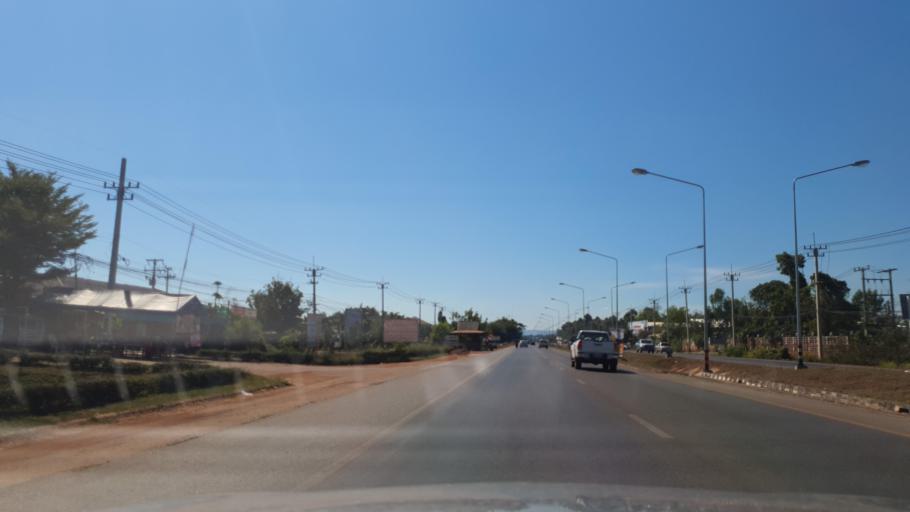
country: TH
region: Sakon Nakhon
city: Sakon Nakhon
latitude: 17.2250
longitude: 104.1061
